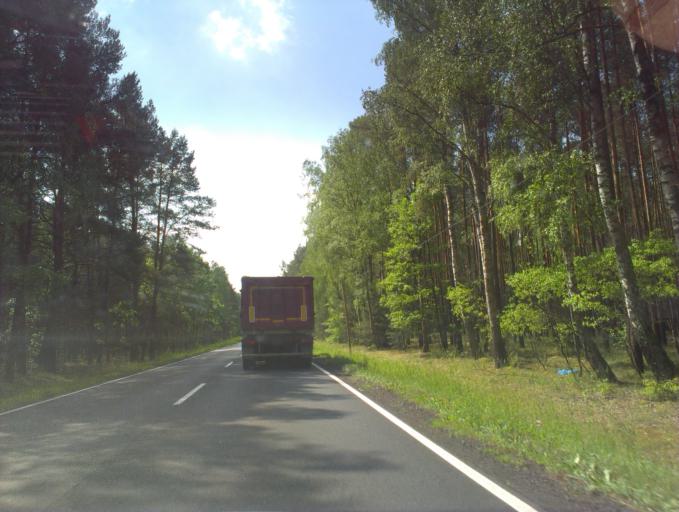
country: PL
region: Greater Poland Voivodeship
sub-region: Powiat zlotowski
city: Tarnowka
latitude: 53.2834
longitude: 16.7824
